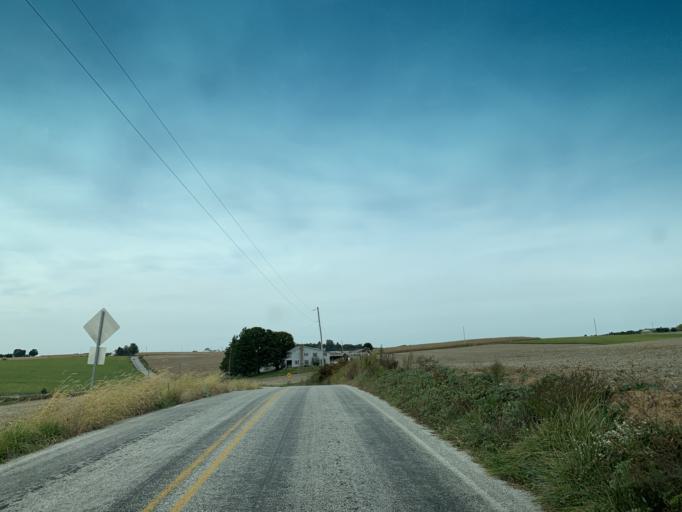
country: US
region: Pennsylvania
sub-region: York County
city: Stewartstown
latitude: 39.8034
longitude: -76.5157
